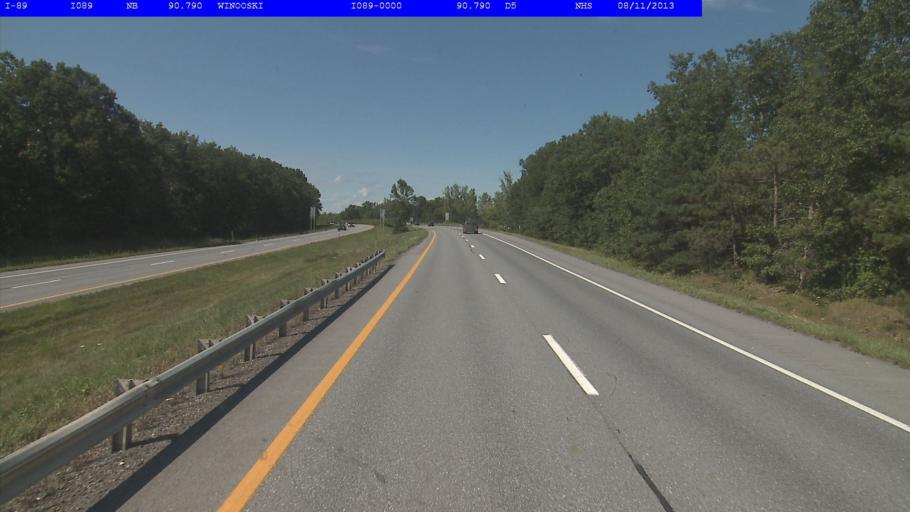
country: US
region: Vermont
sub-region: Chittenden County
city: Winooski
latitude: 44.4979
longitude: -73.1735
